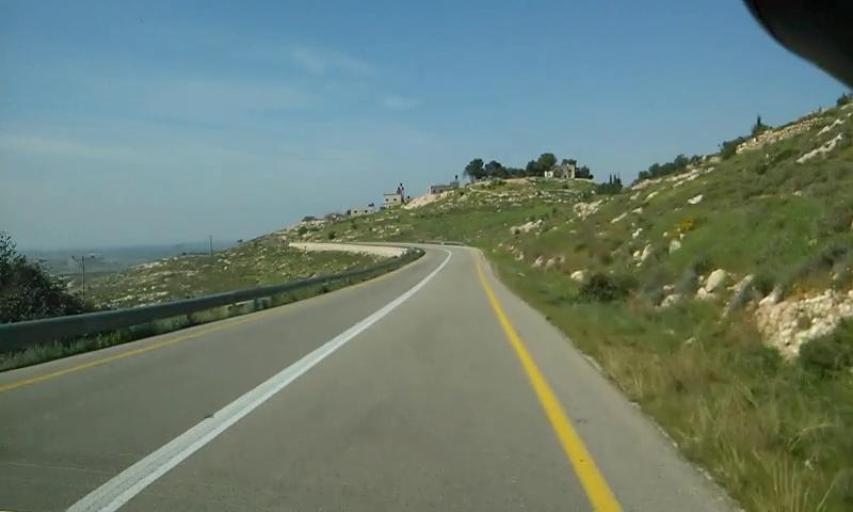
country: PS
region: West Bank
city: Surif
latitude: 31.6728
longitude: 35.0856
